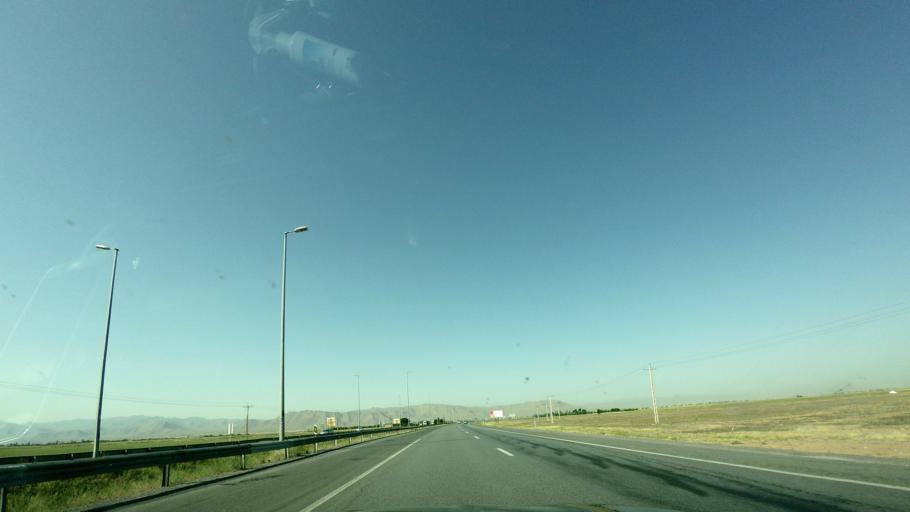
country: IR
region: Markazi
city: Ashtian
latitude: 34.1899
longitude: 50.0536
